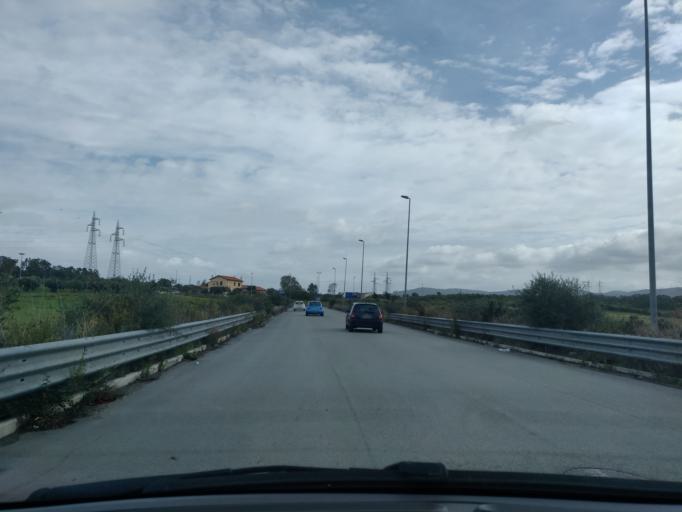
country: IT
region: Latium
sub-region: Citta metropolitana di Roma Capitale
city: Aurelia
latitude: 42.1311
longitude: 11.7741
